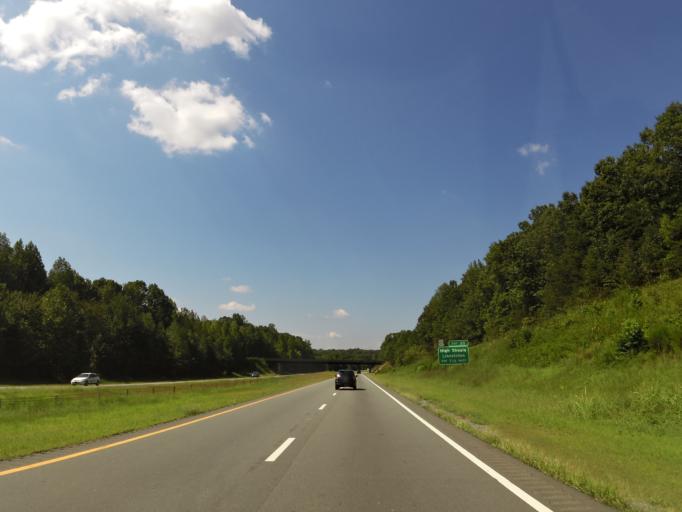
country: US
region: North Carolina
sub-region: Gaston County
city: Dallas
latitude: 35.3898
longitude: -81.2066
